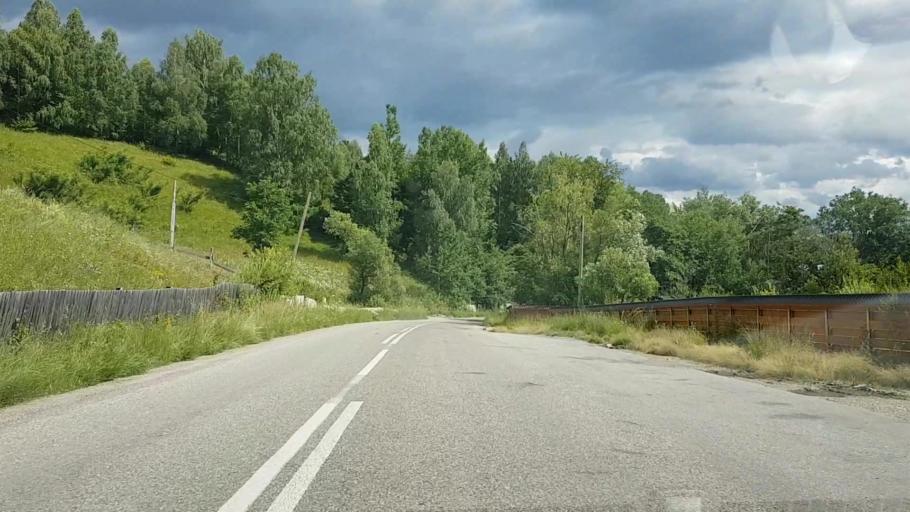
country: RO
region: Neamt
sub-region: Comuna Ceahlau
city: Ceahlau
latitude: 47.0661
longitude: 25.9614
